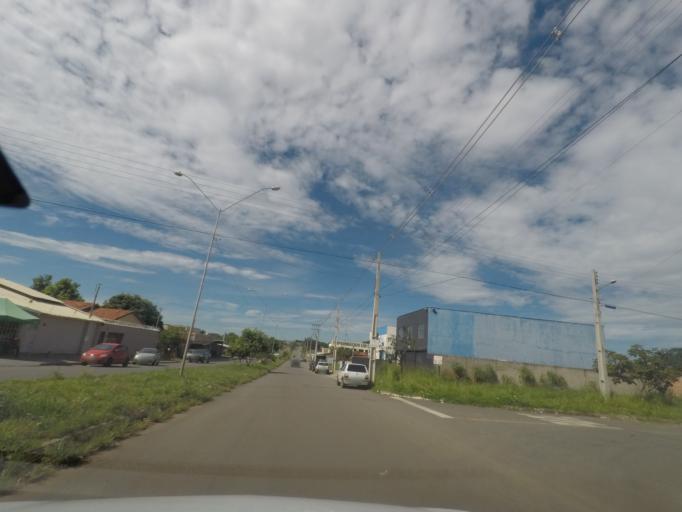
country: BR
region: Goias
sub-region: Aparecida De Goiania
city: Aparecida de Goiania
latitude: -16.8149
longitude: -49.2888
